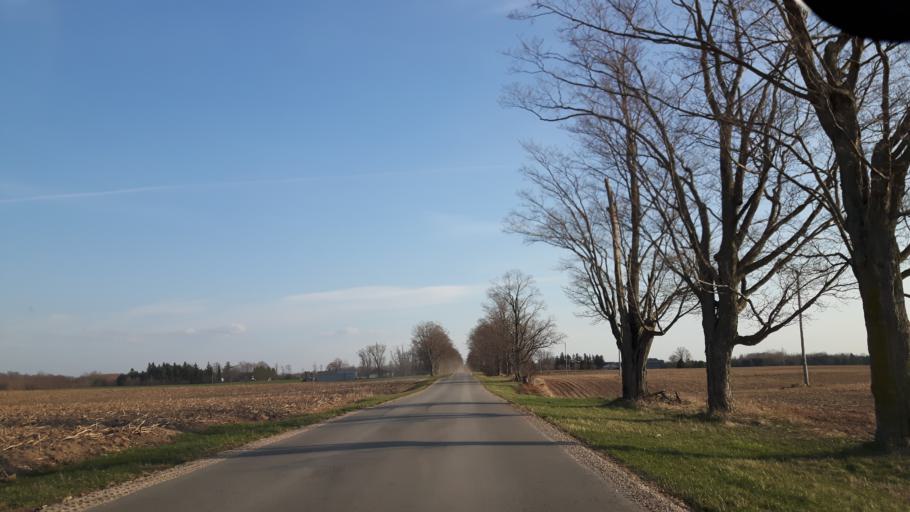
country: CA
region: Ontario
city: Goderich
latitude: 43.6302
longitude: -81.6644
